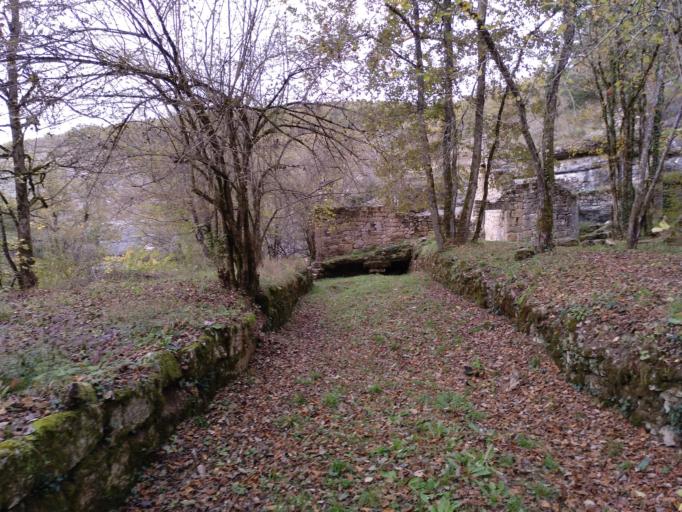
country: FR
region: Midi-Pyrenees
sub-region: Departement du Lot
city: Gramat
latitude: 44.7906
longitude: 1.5836
